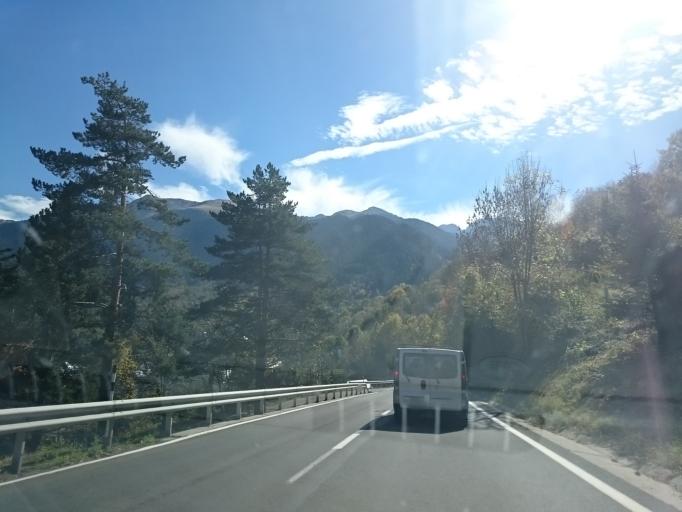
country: ES
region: Catalonia
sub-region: Provincia de Lleida
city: Vielha
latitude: 42.7048
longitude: 0.7897
